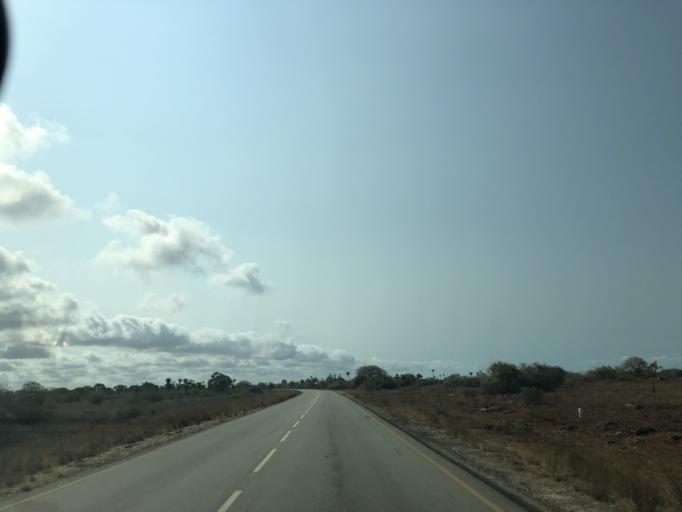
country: AO
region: Luanda
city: Luanda
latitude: -9.7052
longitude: 13.2162
